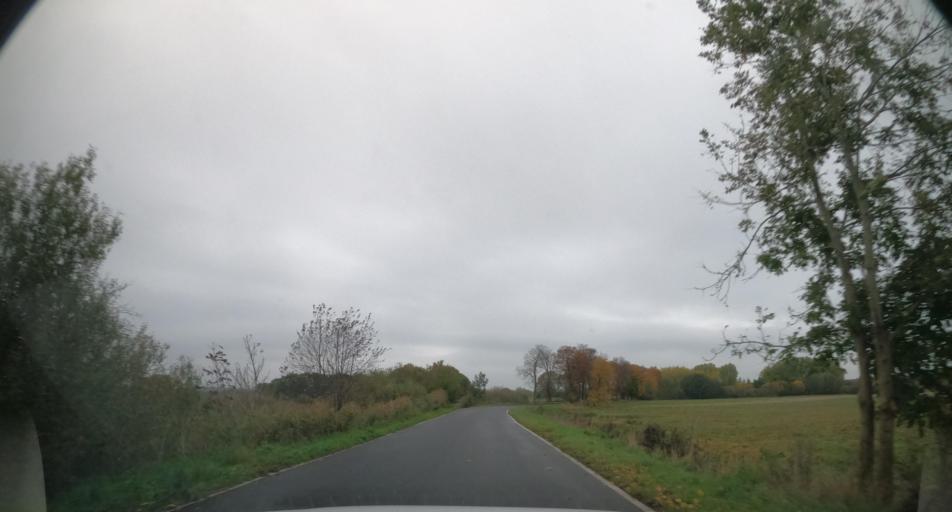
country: PL
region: West Pomeranian Voivodeship
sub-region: Powiat kamienski
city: Wolin
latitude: 53.9263
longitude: 14.6080
